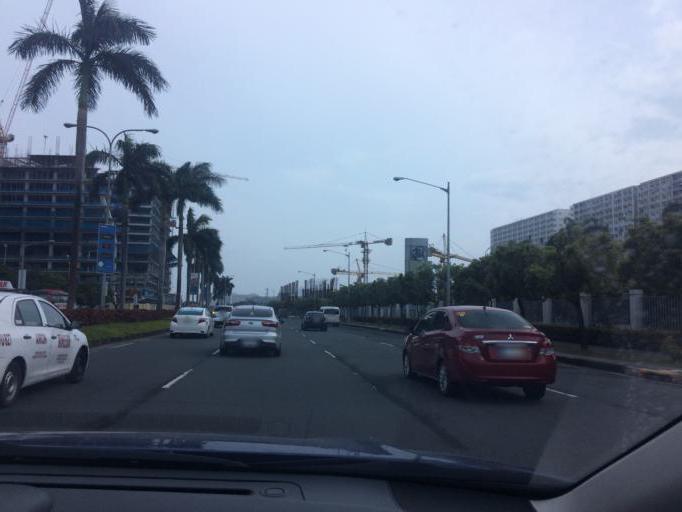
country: PH
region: Metro Manila
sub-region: City of Manila
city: Port Area
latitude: 14.5385
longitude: 120.9840
